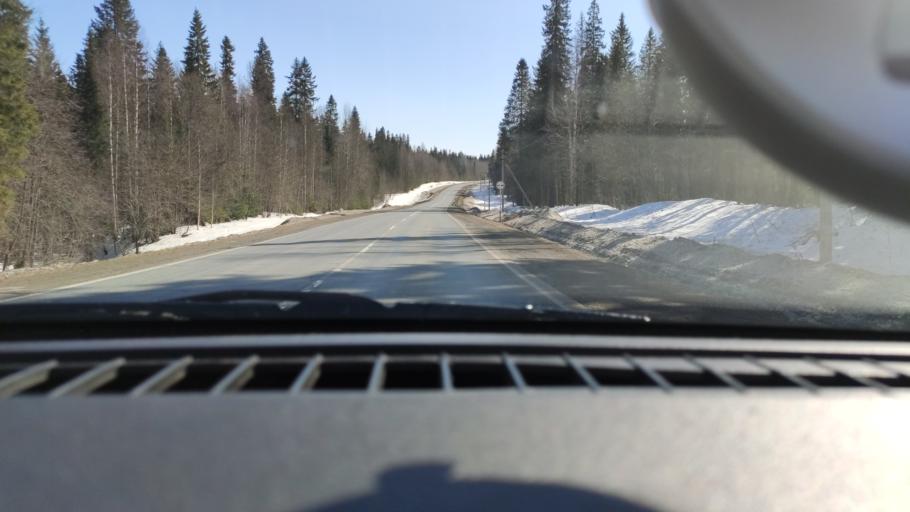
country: RU
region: Perm
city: Perm
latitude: 58.2045
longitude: 56.2000
